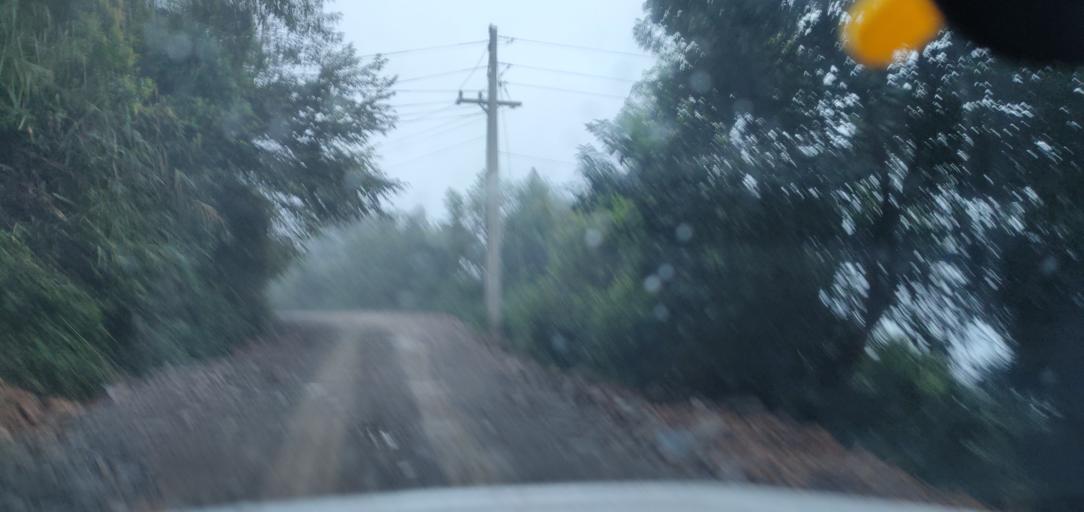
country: LA
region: Phongsali
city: Phongsali
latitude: 21.4209
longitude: 102.2519
